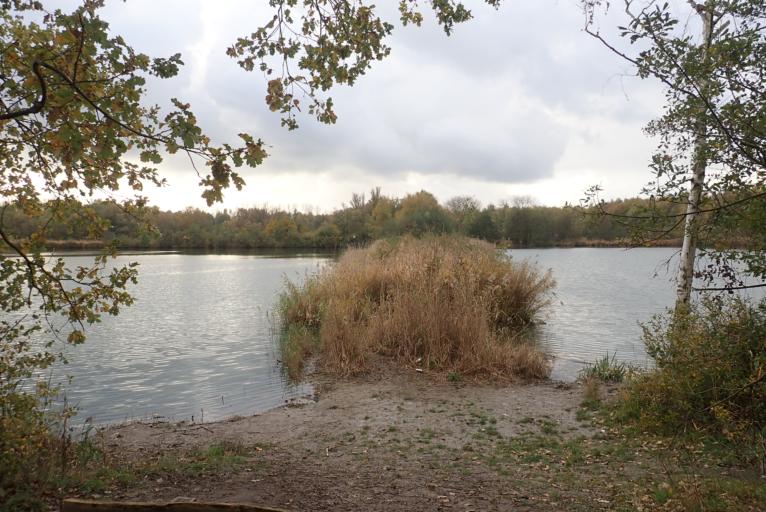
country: BE
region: Flanders
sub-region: Provincie Antwerpen
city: Niel
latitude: 51.1061
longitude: 4.3493
